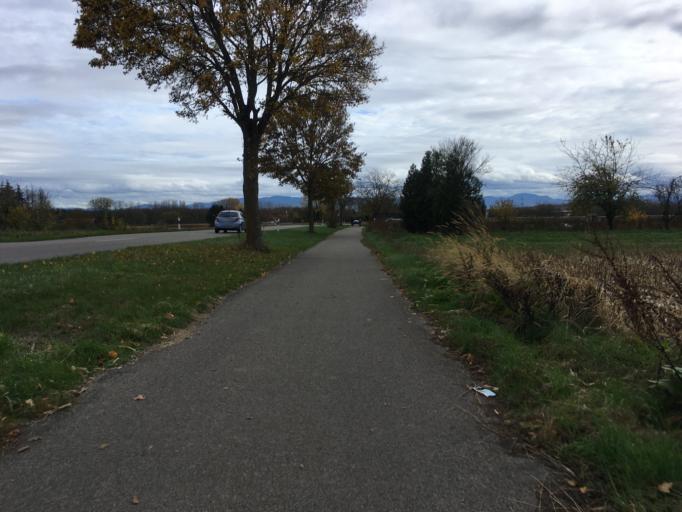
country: DE
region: Baden-Wuerttemberg
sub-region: Freiburg Region
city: Ihringen
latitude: 48.0351
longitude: 7.6519
